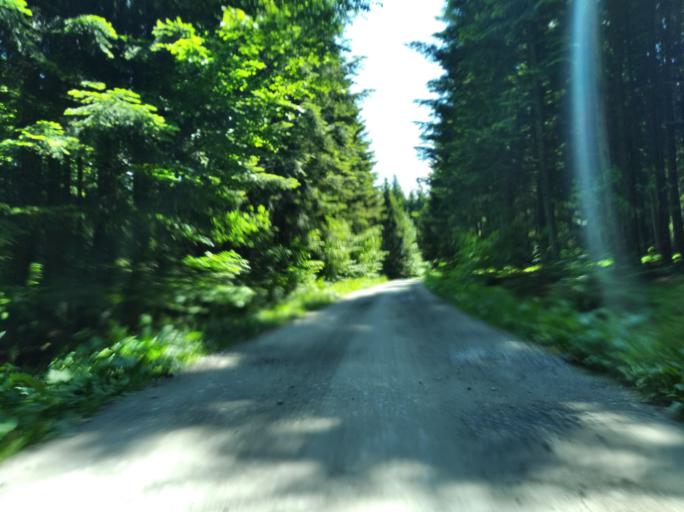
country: PL
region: Subcarpathian Voivodeship
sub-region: Powiat ropczycko-sedziszowski
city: Zagorzyce
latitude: 49.9758
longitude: 21.6738
